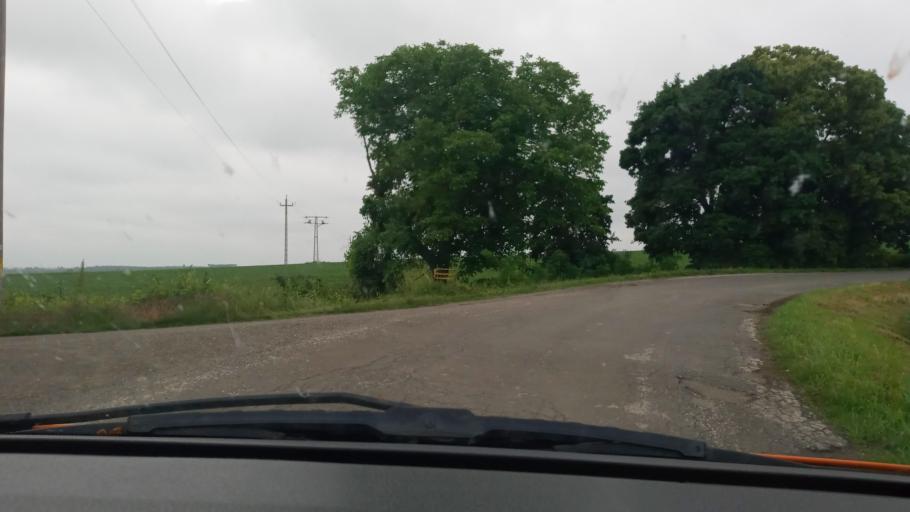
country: HU
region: Baranya
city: Szigetvar
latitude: 46.0755
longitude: 17.8606
